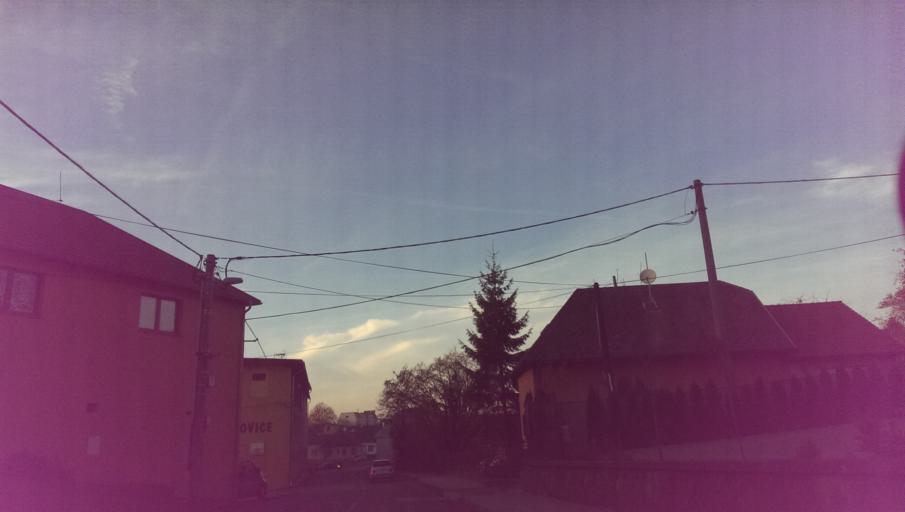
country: CZ
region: Zlin
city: Tecovice
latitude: 49.2052
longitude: 17.5979
